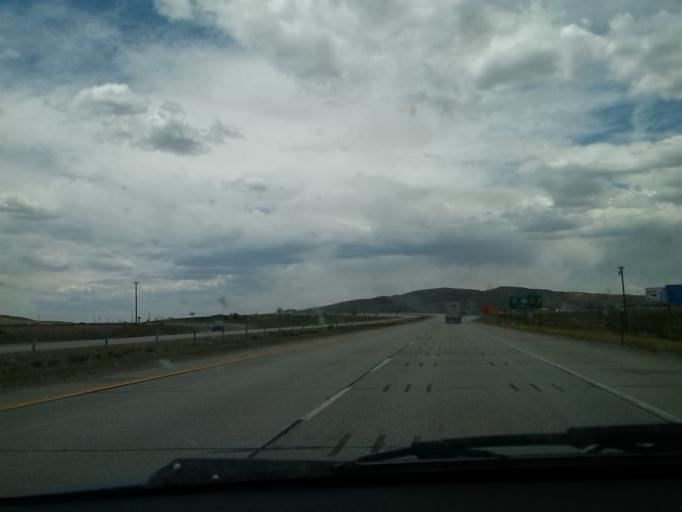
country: US
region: Wyoming
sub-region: Carbon County
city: Rawlins
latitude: 41.7883
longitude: -107.1905
